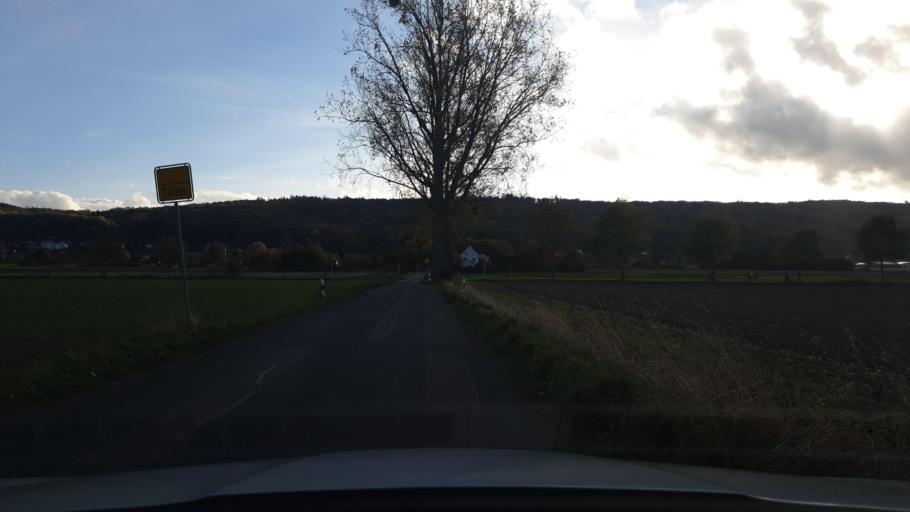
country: DE
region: North Rhine-Westphalia
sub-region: Regierungsbezirk Detmold
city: Minden
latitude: 52.2671
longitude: 8.8593
